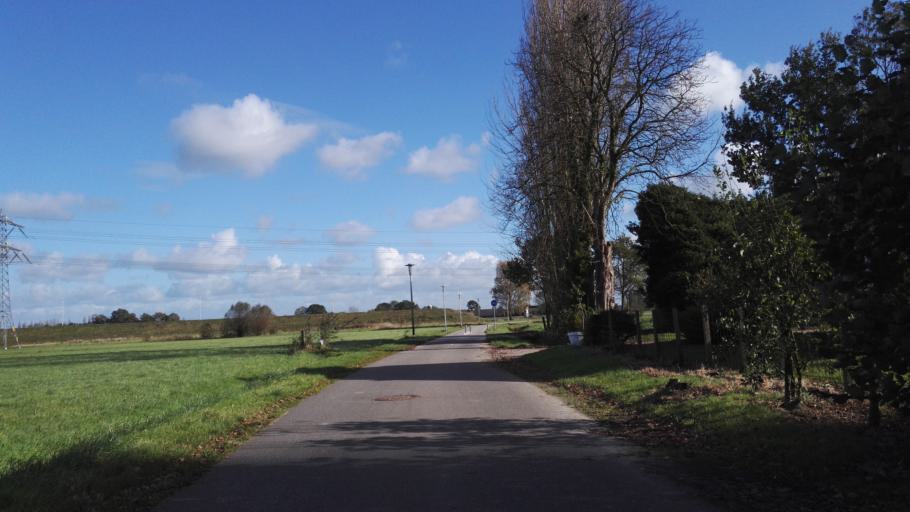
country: NL
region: Gelderland
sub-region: Gemeente Apeldoorn
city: Apeldoorn
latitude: 52.2385
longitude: 6.0066
